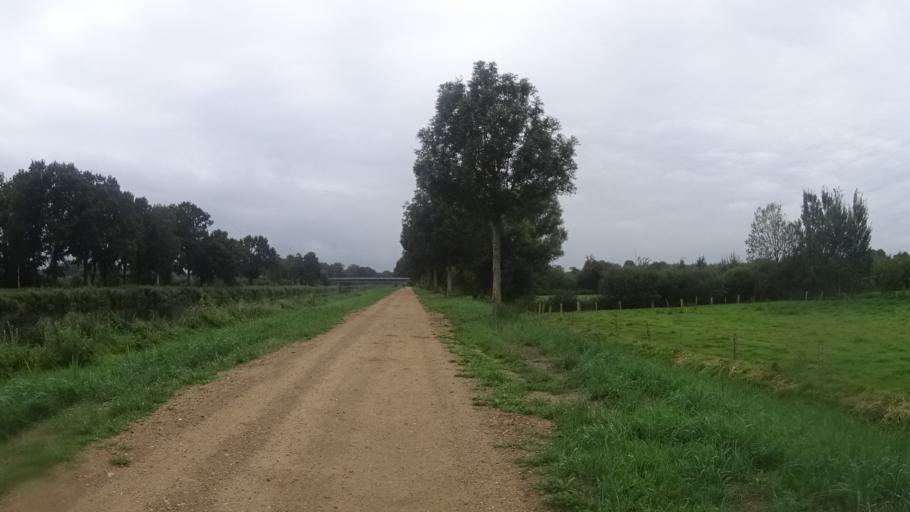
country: DE
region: Schleswig-Holstein
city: Buchen
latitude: 53.4828
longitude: 10.6307
